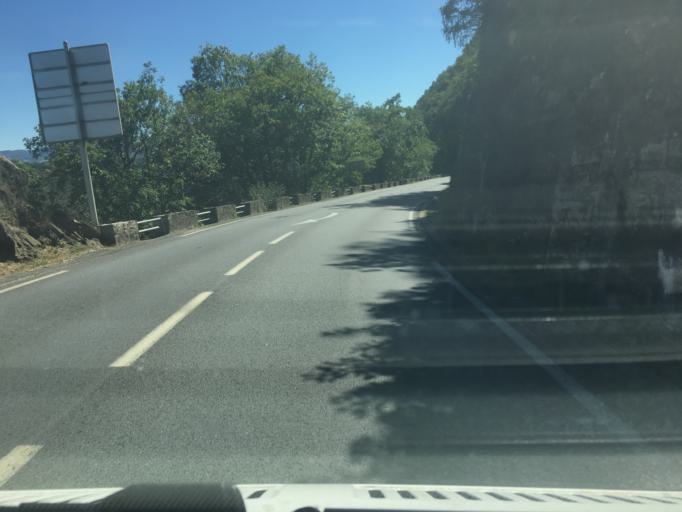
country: FR
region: Limousin
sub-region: Departement de la Correze
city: Bort-les-Orgues
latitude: 45.4101
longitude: 2.4995
